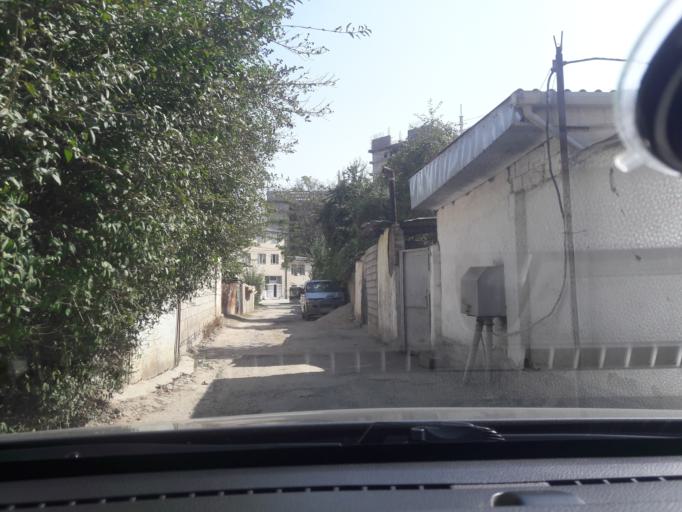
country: TJ
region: Dushanbe
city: Dushanbe
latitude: 38.5766
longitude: 68.7996
